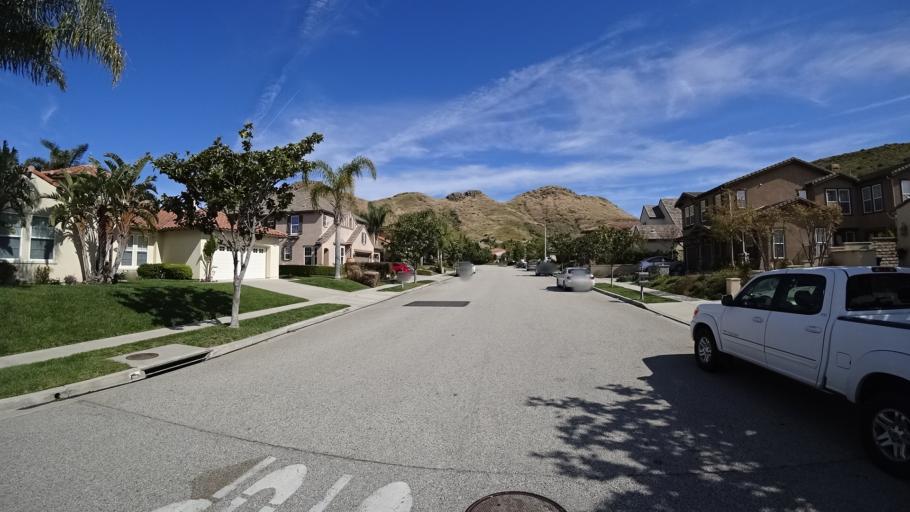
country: US
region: California
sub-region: Ventura County
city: Casa Conejo
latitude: 34.1756
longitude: -118.9726
